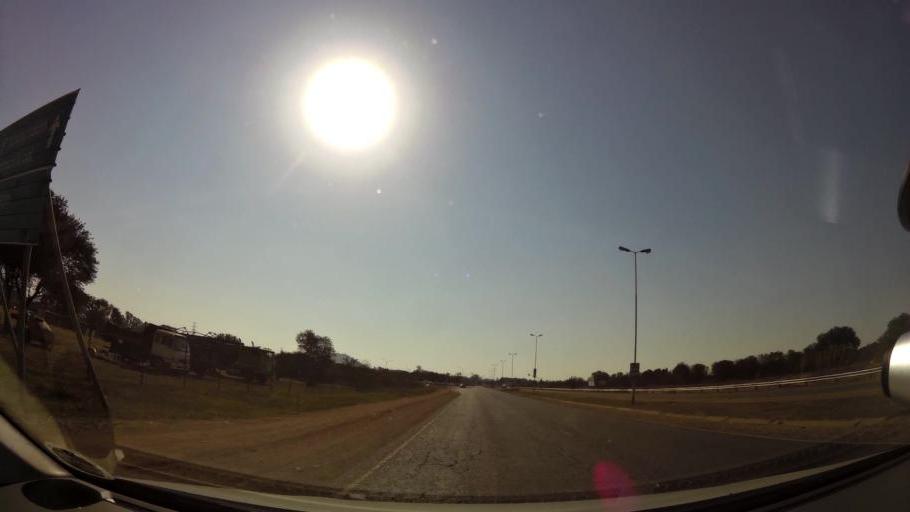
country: ZA
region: Gauteng
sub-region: City of Tshwane Metropolitan Municipality
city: Pretoria
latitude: -25.6628
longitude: 28.1918
